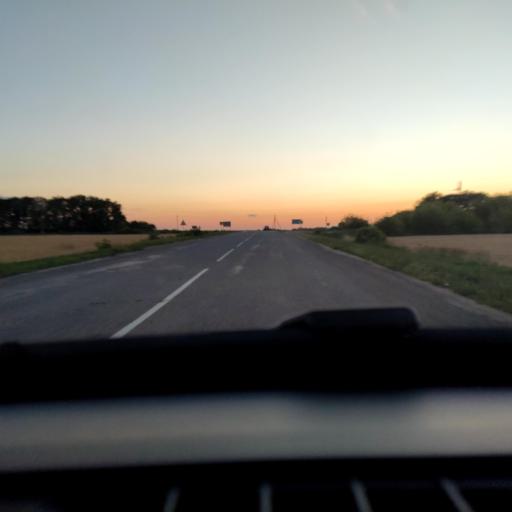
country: RU
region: Lipetsk
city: Zadonsk
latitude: 52.2991
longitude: 38.8051
